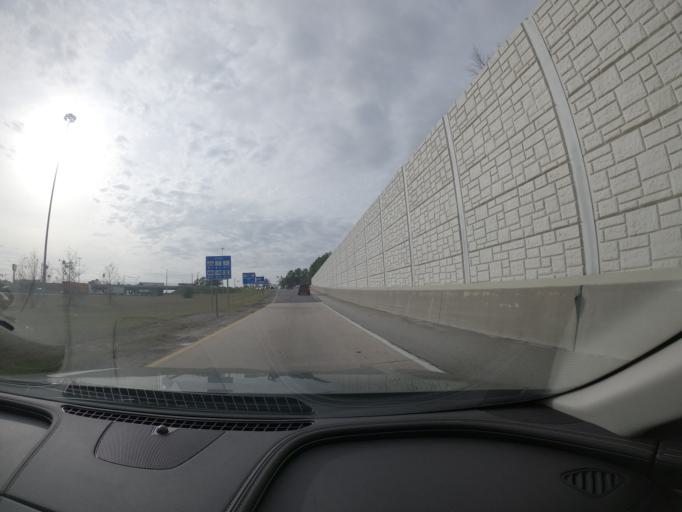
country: US
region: Georgia
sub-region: Columbia County
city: Evans
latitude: 33.4836
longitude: -82.1281
